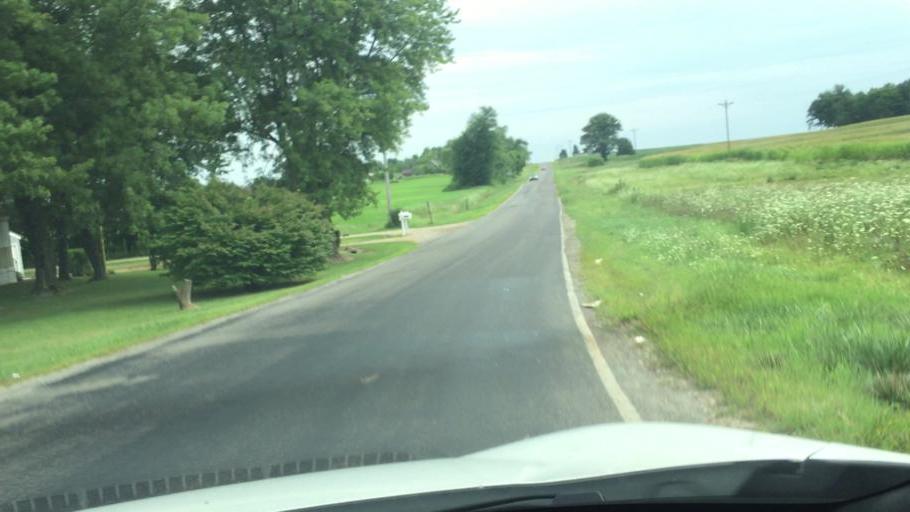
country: US
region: Ohio
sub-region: Champaign County
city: Mechanicsburg
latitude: 40.0470
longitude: -83.6564
